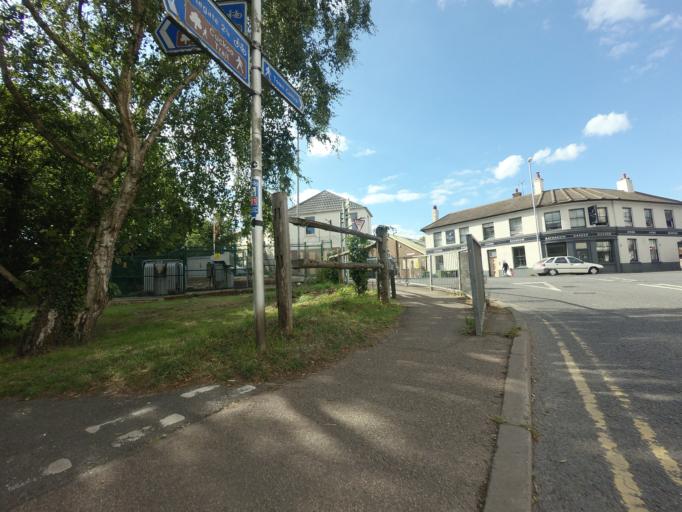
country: GB
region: England
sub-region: East Sussex
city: Hailsham
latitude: 50.8616
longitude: 0.2575
